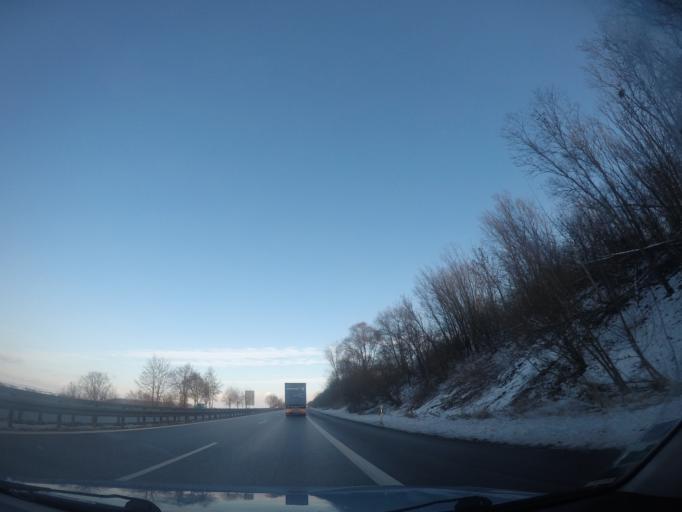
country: DE
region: Baden-Wuerttemberg
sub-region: Tuebingen Region
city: Laupheim
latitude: 48.2428
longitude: 9.8791
